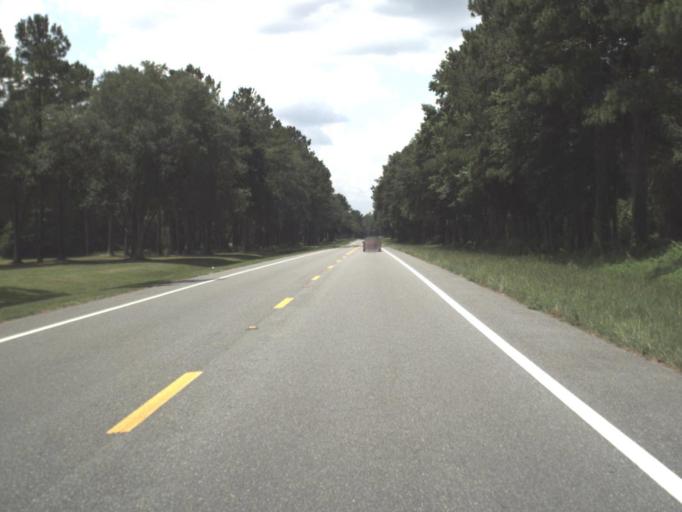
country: US
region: Florida
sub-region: Columbia County
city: Five Points
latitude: 30.2795
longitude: -82.6988
